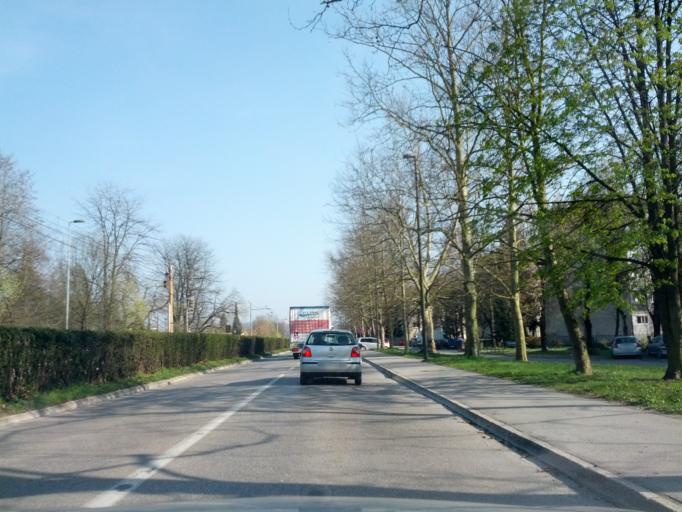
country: SI
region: Ljubljana
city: Ljubljana
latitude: 46.0768
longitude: 14.4901
